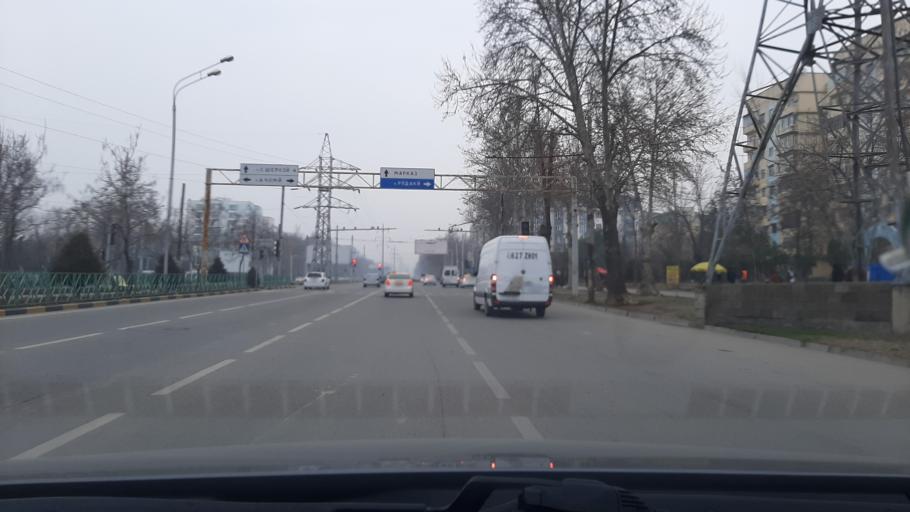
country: TJ
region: Dushanbe
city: Dushanbe
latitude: 38.5236
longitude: 68.7621
